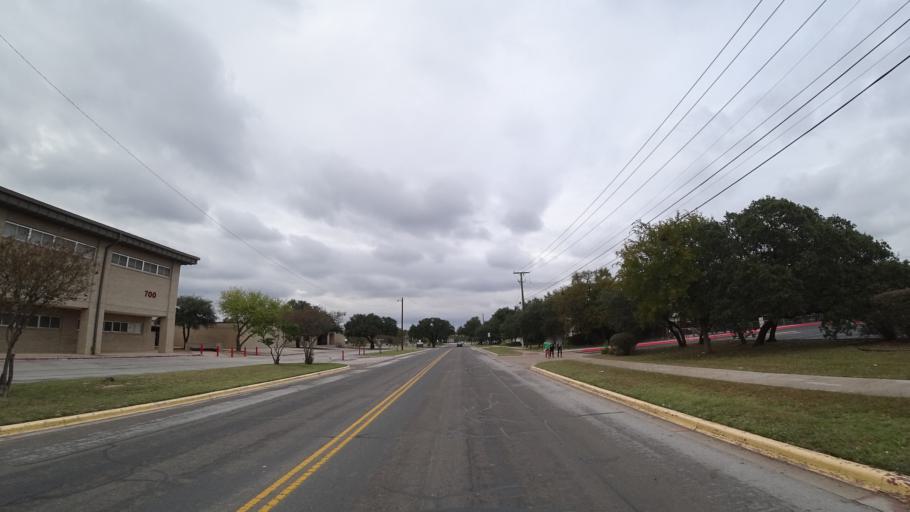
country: US
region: Texas
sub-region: Williamson County
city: Round Rock
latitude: 30.5089
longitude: -97.6947
